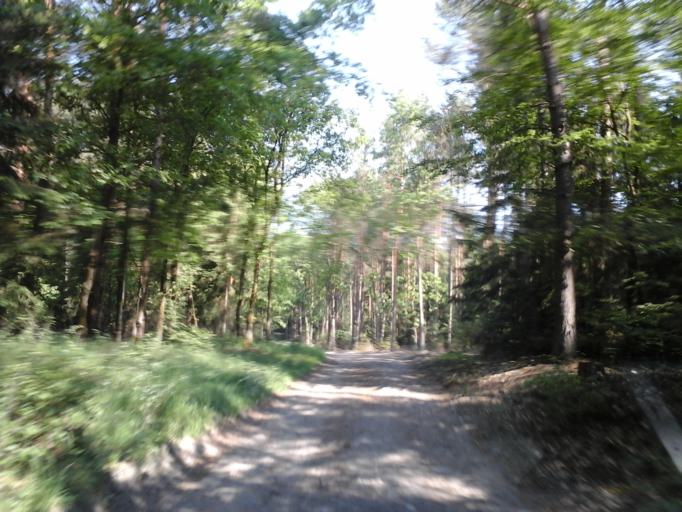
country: PL
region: West Pomeranian Voivodeship
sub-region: Powiat choszczenski
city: Recz
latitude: 53.3283
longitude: 15.5270
